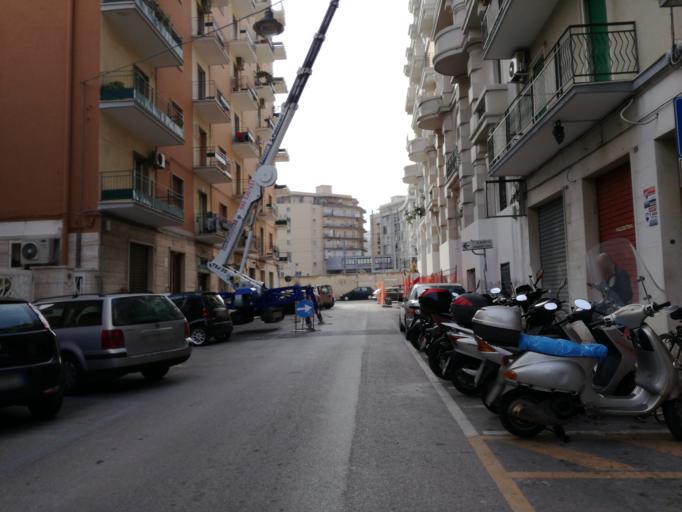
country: IT
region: Apulia
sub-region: Provincia di Bari
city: Bari
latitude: 41.1190
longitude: 16.8787
